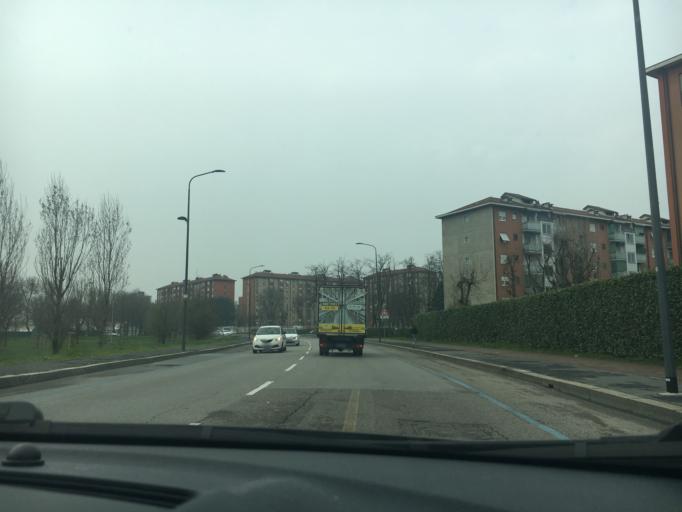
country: IT
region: Lombardy
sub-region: Citta metropolitana di Milano
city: Pero
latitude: 45.4933
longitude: 9.1070
